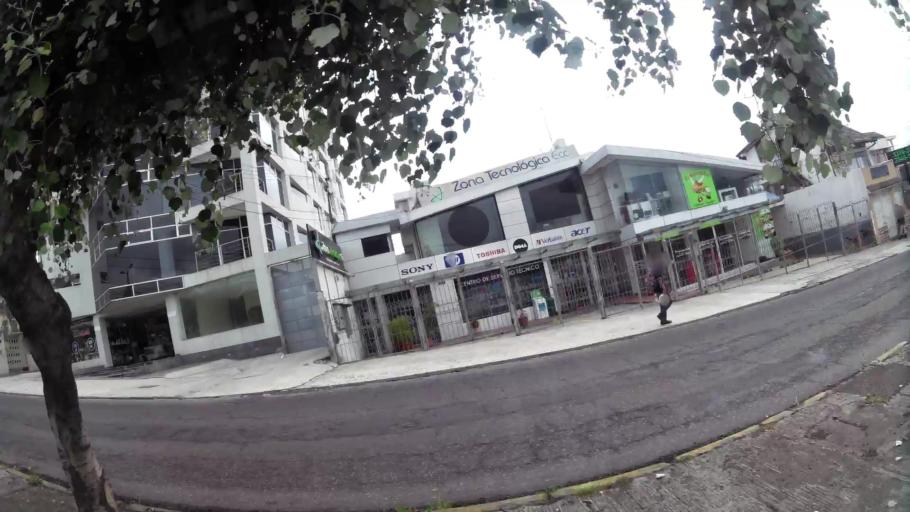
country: EC
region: Pichincha
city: Quito
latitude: -0.1599
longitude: -78.4907
